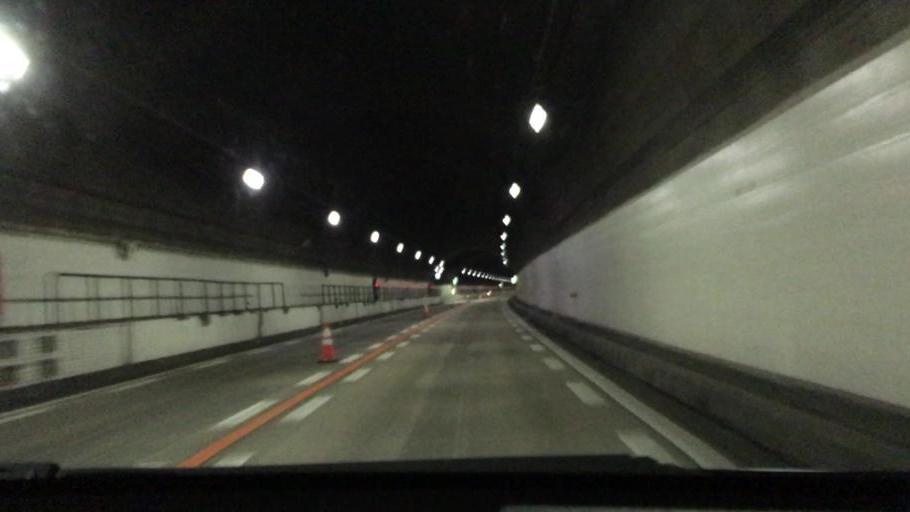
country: JP
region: Yamaguchi
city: Ogori-shimogo
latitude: 34.1047
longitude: 131.4496
